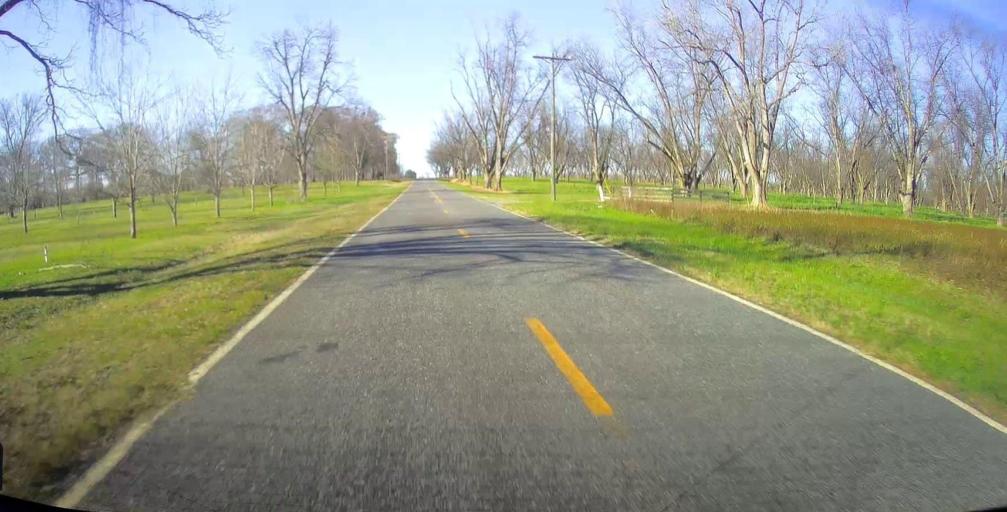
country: US
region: Georgia
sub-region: Peach County
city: Fort Valley
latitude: 32.5987
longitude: -83.8524
